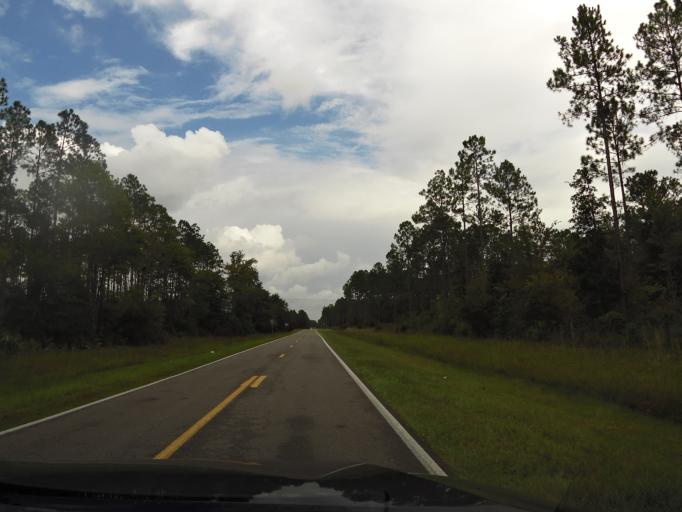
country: US
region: Florida
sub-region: Duval County
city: Baldwin
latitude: 30.3752
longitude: -81.9373
